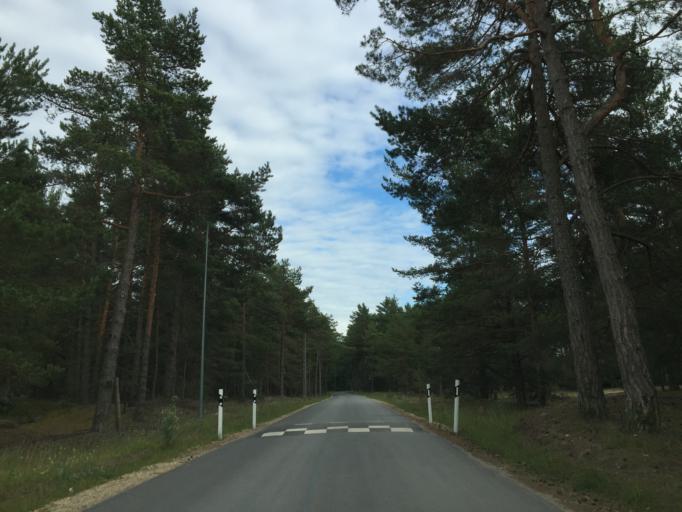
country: LV
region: Carnikava
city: Carnikava
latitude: 57.1357
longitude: 24.2472
